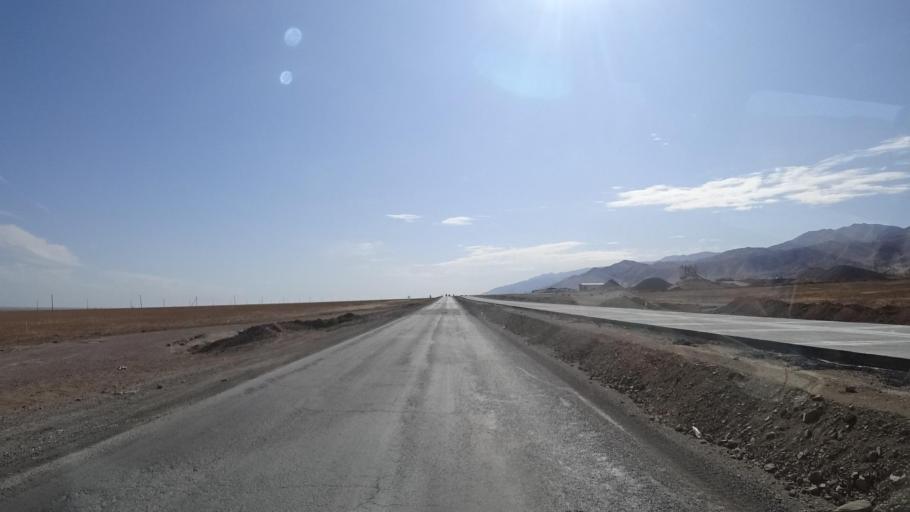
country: KG
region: Chuy
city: Ivanovka
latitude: 43.3924
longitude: 75.1365
